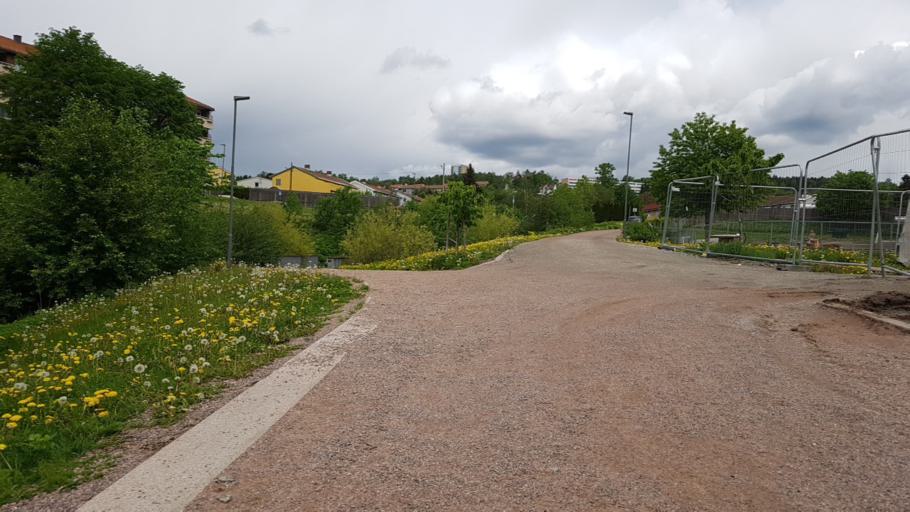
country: NO
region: Oslo
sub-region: Oslo
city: Oslo
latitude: 59.9394
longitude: 10.8217
